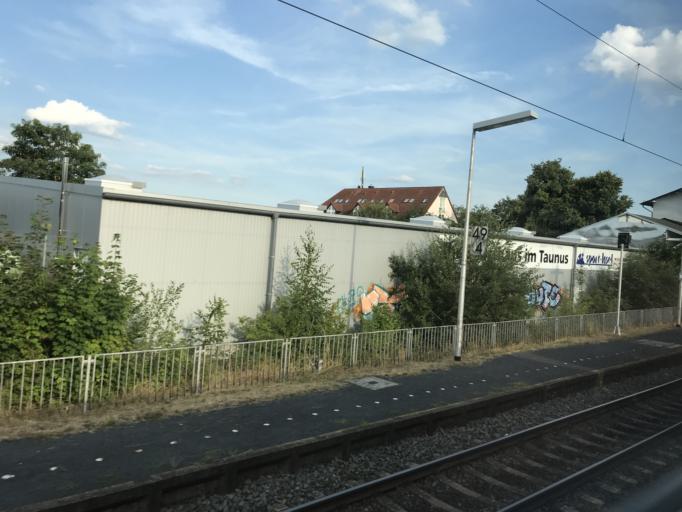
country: DE
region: Hesse
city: Bad Camberg
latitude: 50.2972
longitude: 8.2547
